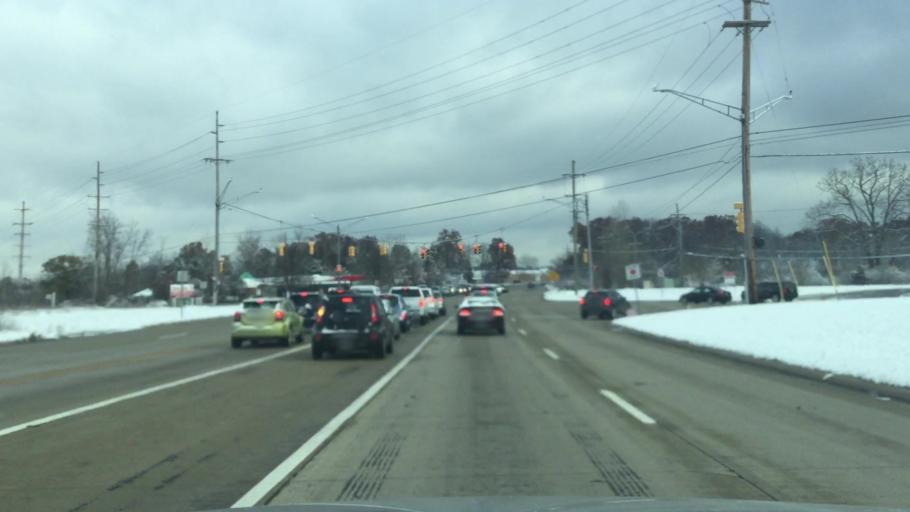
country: US
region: Michigan
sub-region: Oakland County
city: Wolverine Lake
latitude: 42.5593
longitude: -83.4400
